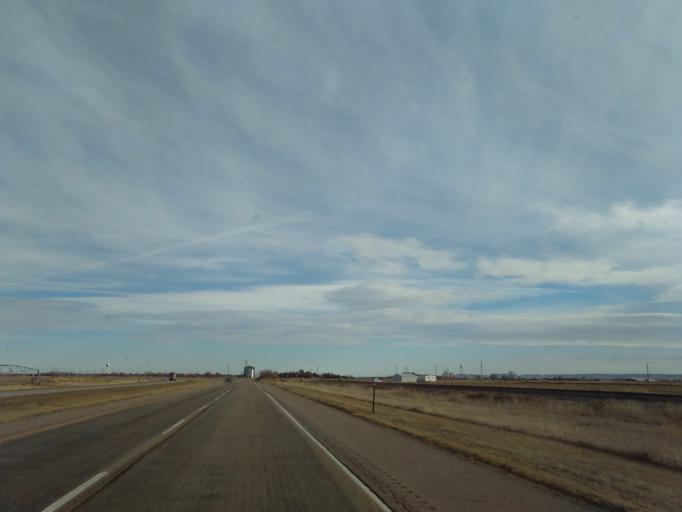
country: US
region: Nebraska
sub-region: Scotts Bluff County
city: Gering
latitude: 41.8170
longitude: -103.5320
